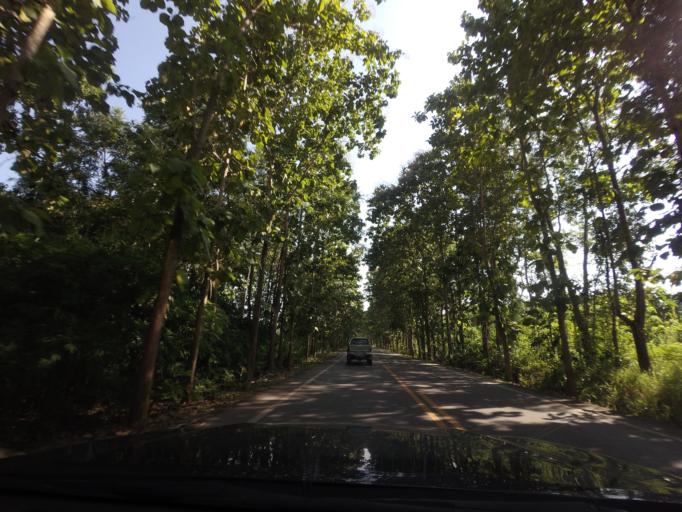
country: TH
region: Nan
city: Nan
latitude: 18.8247
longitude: 100.8079
